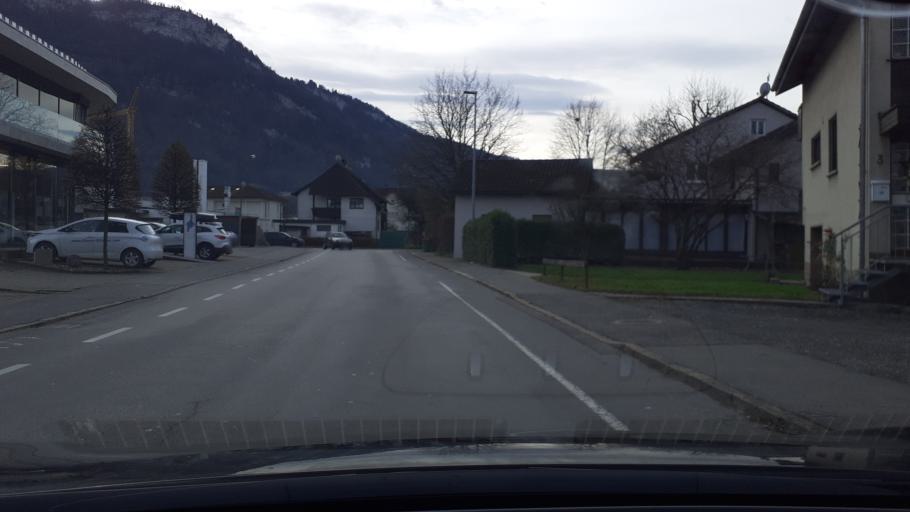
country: AT
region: Vorarlberg
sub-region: Politischer Bezirk Dornbirn
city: Hohenems
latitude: 47.3643
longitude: 9.6768
